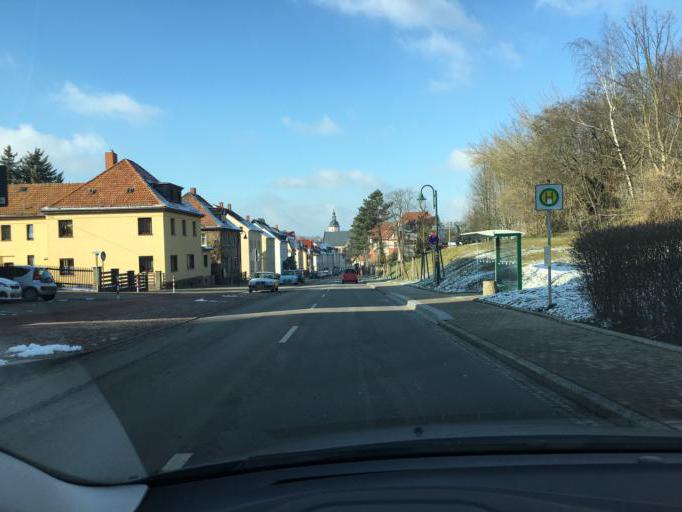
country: DE
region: Saxony
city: Penig
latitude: 50.9278
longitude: 12.7091
